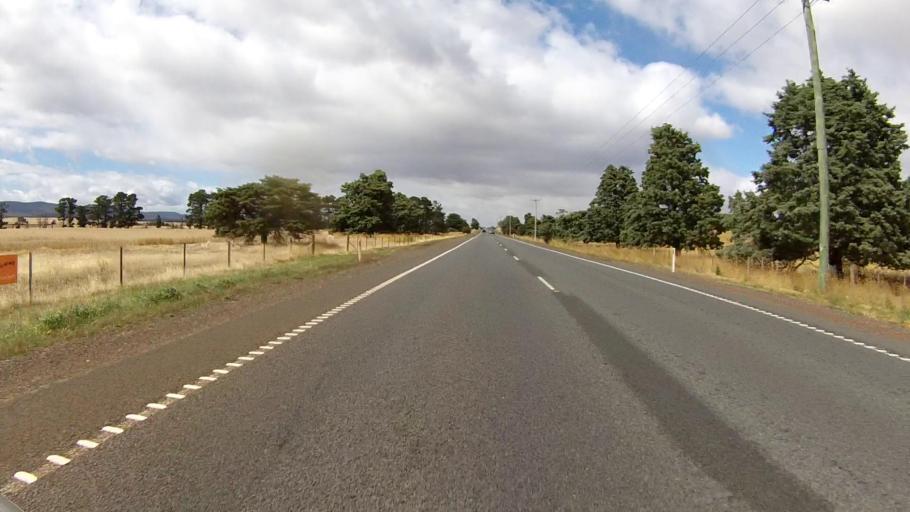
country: AU
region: Tasmania
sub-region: Northern Midlands
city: Evandale
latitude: -41.9492
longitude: 147.4943
